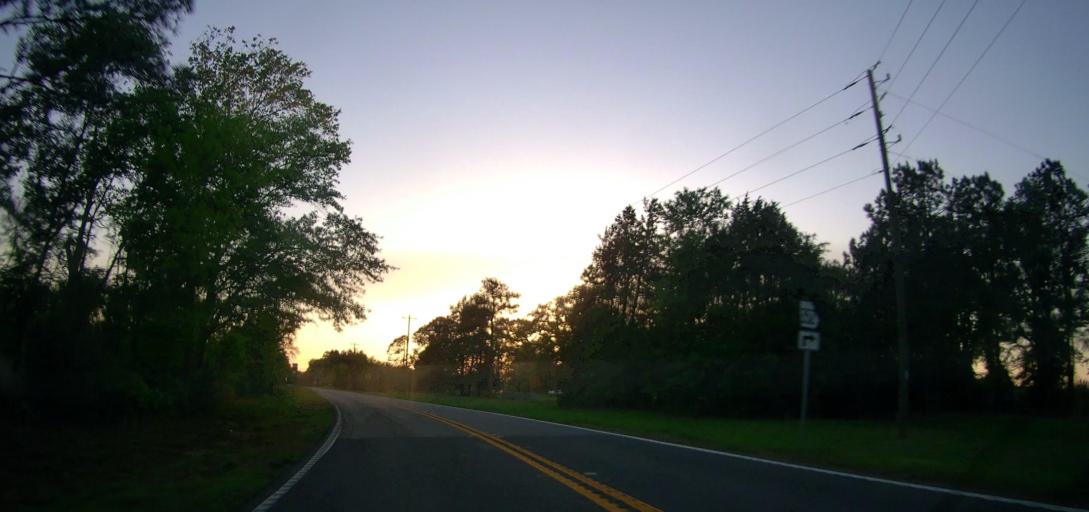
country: US
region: Georgia
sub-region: Marion County
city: Buena Vista
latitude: 32.3722
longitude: -84.5547
